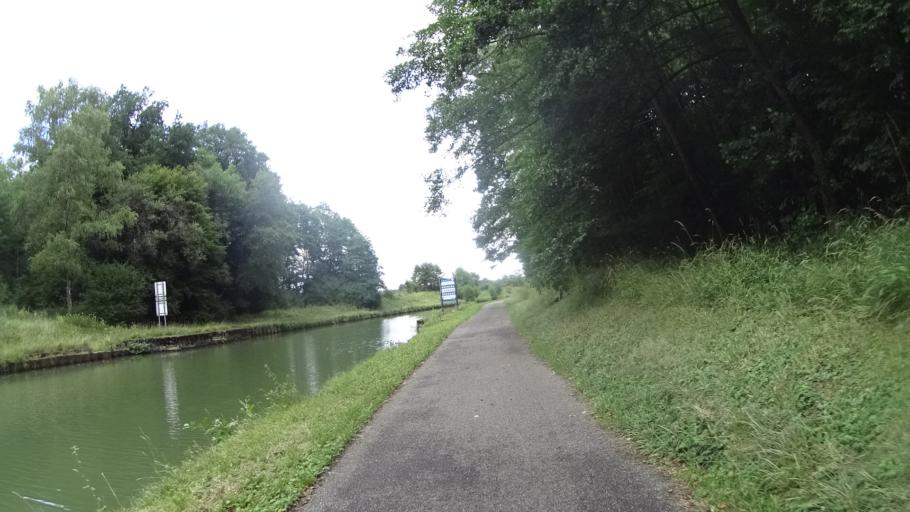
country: FR
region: Lorraine
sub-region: Departement de la Moselle
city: Lorquin
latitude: 48.7029
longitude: 6.8667
